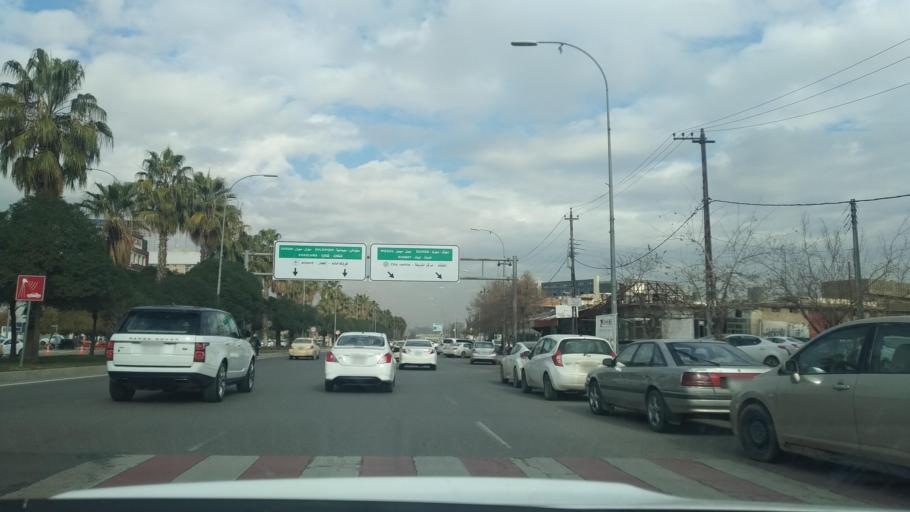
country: IQ
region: Arbil
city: Erbil
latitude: 36.1855
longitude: 43.9942
